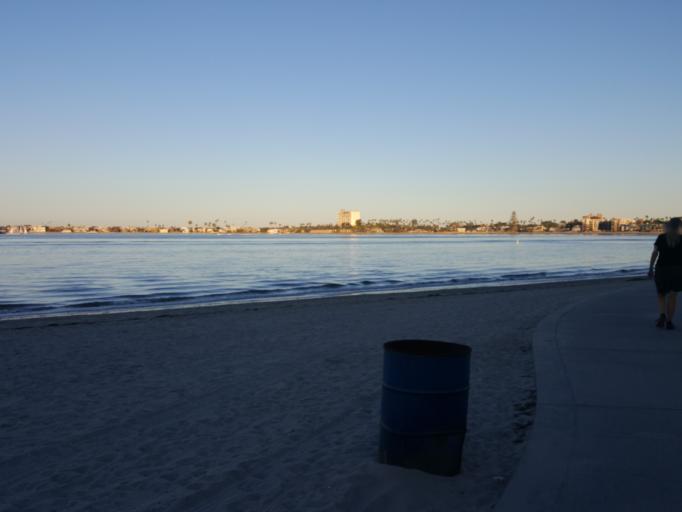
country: US
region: California
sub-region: San Diego County
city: La Jolla
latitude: 32.7857
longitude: -117.2401
